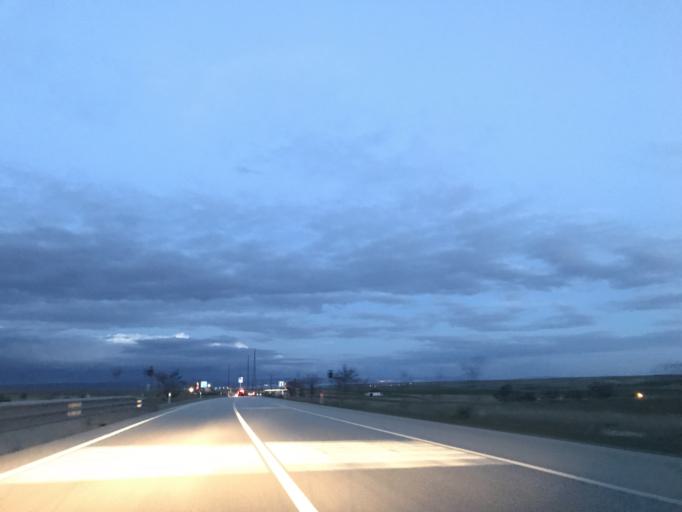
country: TR
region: Konya
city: Kulu
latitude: 39.1598
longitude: 33.1978
